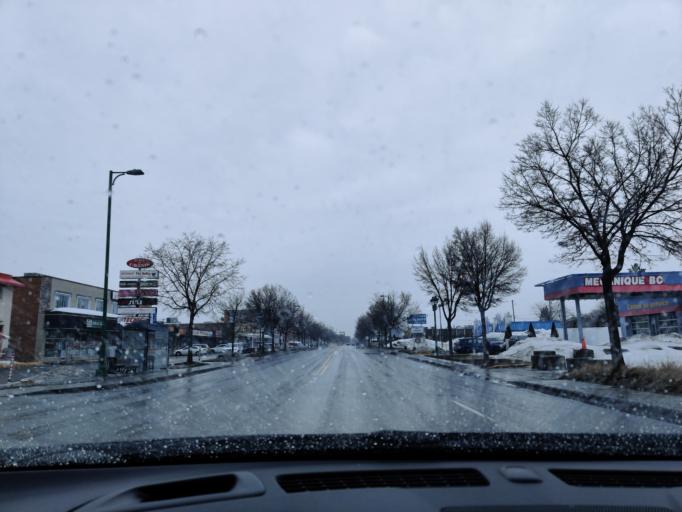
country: CA
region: Quebec
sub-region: Laval
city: Laval
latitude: 45.5463
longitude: -73.7541
